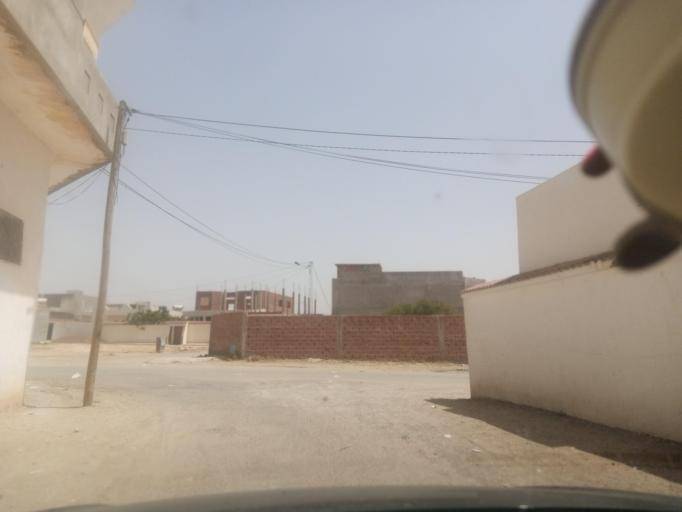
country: TN
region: Al Qasrayn
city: Kasserine
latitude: 35.2122
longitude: 8.8977
